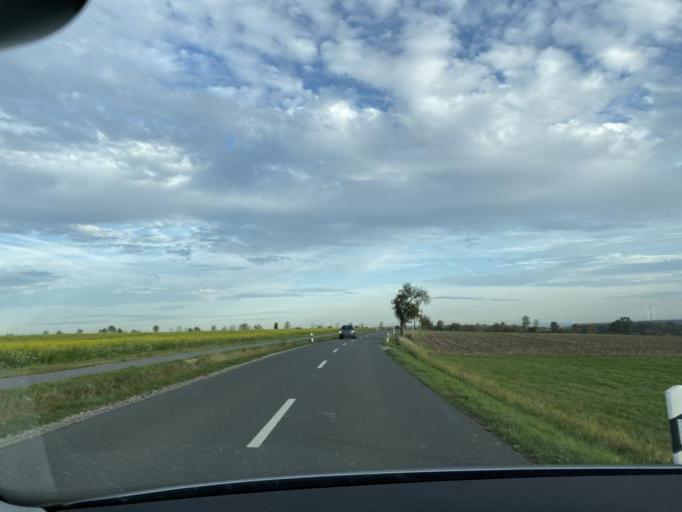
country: DE
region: Bavaria
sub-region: Regierungsbezirk Mittelfranken
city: Puschendorf
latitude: 49.5319
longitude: 10.8086
